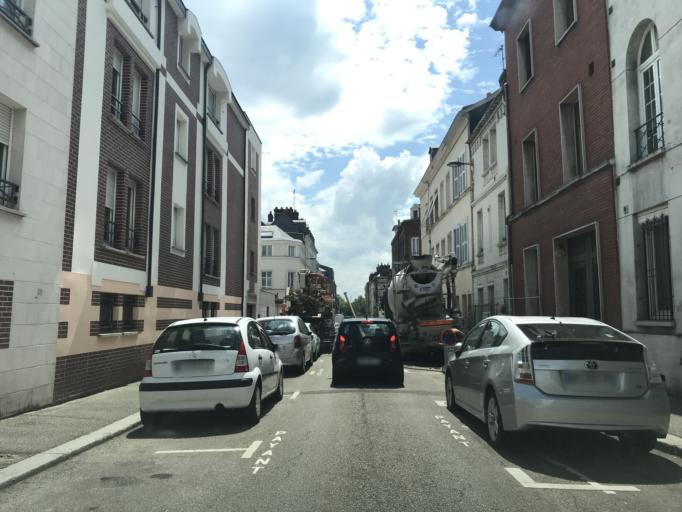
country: FR
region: Haute-Normandie
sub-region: Departement de la Seine-Maritime
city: Rouen
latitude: 49.4442
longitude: 1.0811
